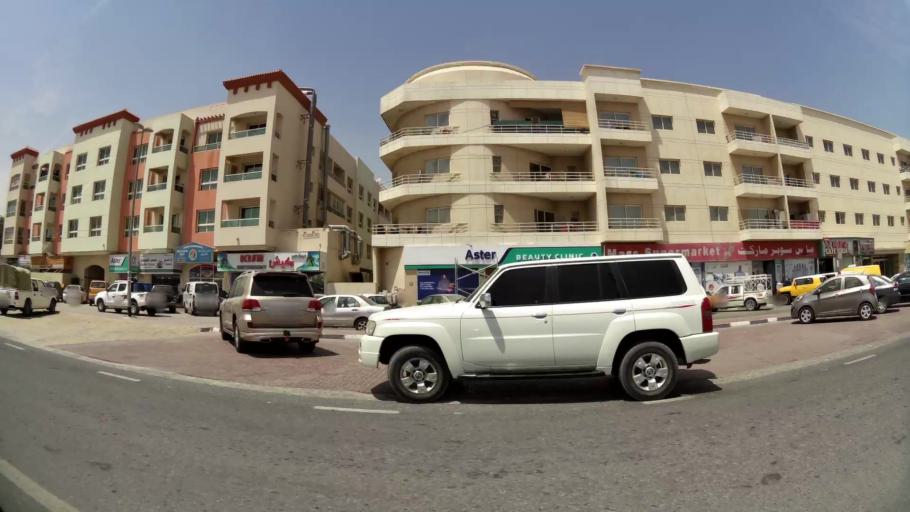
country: AE
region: Ash Shariqah
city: Sharjah
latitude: 25.1934
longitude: 55.4069
